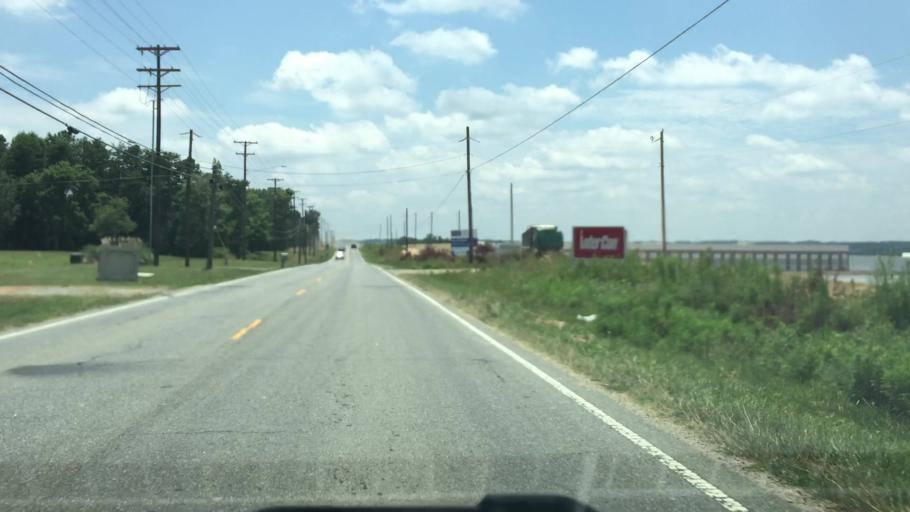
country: US
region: North Carolina
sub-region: Cabarrus County
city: Harrisburg
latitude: 35.4012
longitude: -80.7155
